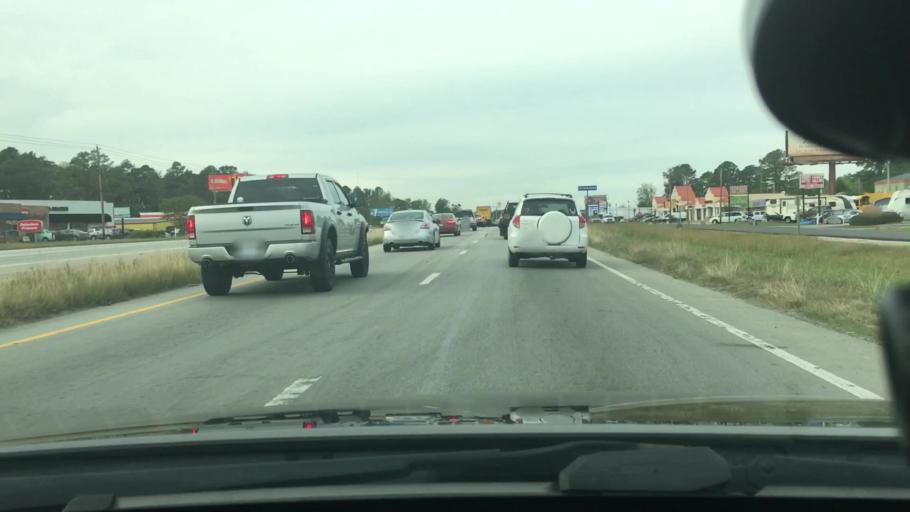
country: US
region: North Carolina
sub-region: Craven County
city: James City
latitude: 35.0750
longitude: -77.0279
